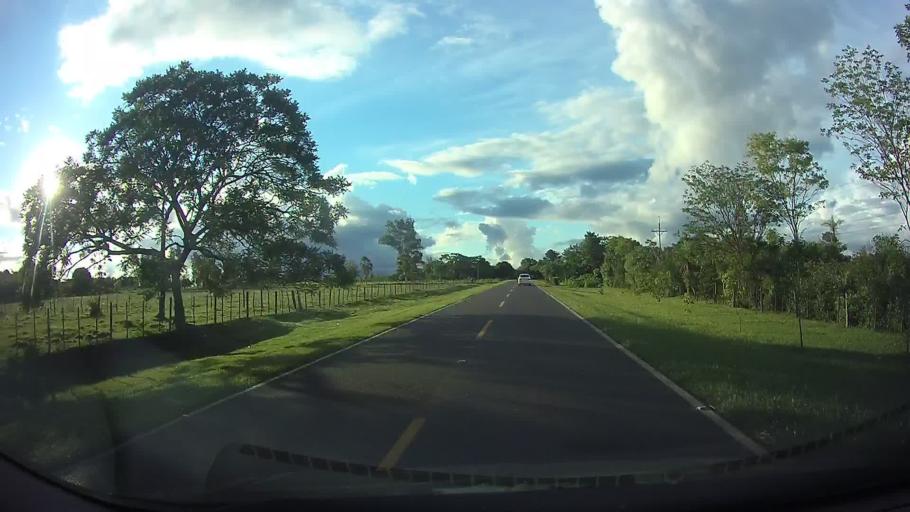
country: PY
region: Paraguari
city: Ybycui
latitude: -25.9838
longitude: -57.0674
